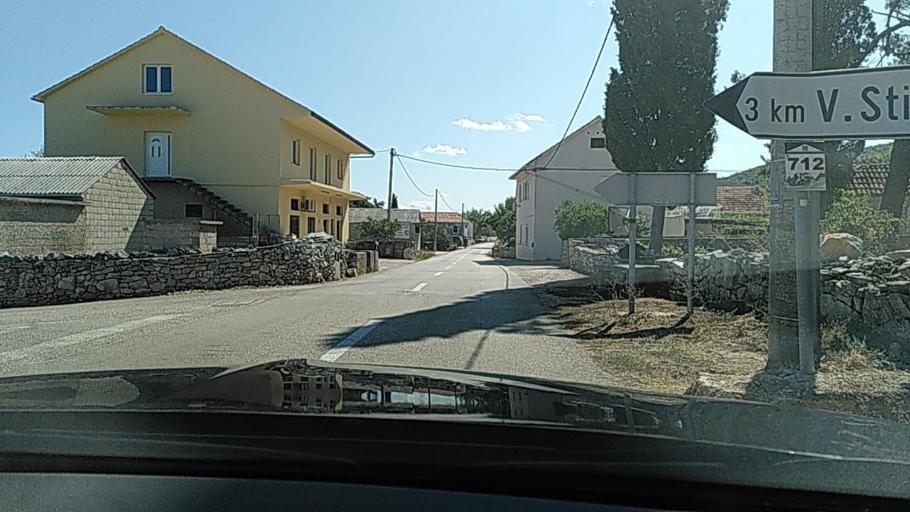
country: HR
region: Splitsko-Dalmatinska
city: Jelsa
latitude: 43.1462
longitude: 16.8317
